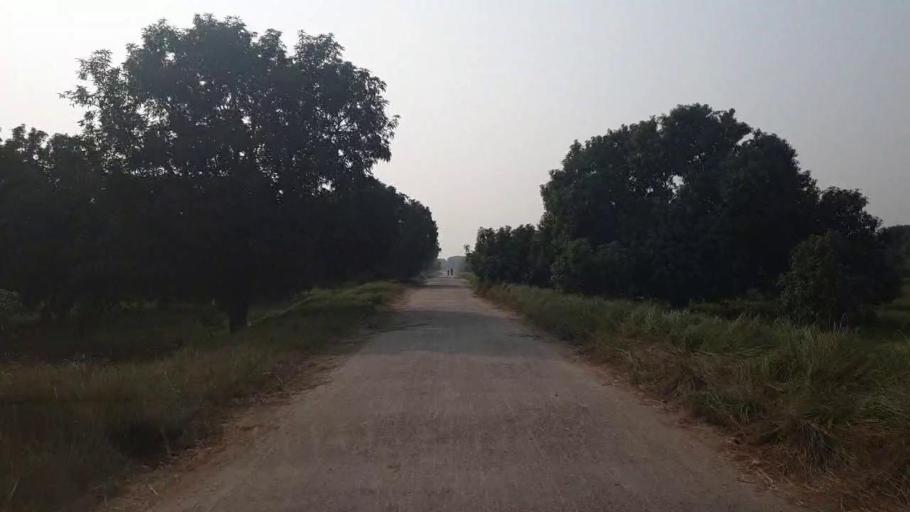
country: PK
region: Sindh
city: Tando Jam
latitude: 25.3287
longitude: 68.5180
